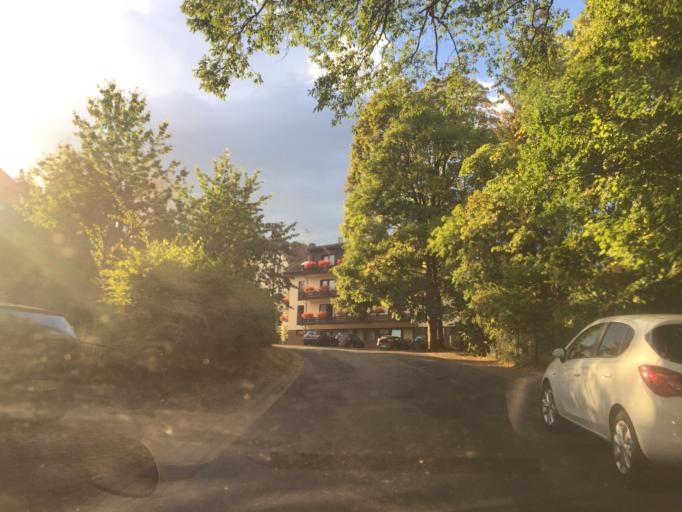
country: DE
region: Lower Saxony
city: Bad Sachsa
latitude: 51.5993
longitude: 10.5545
